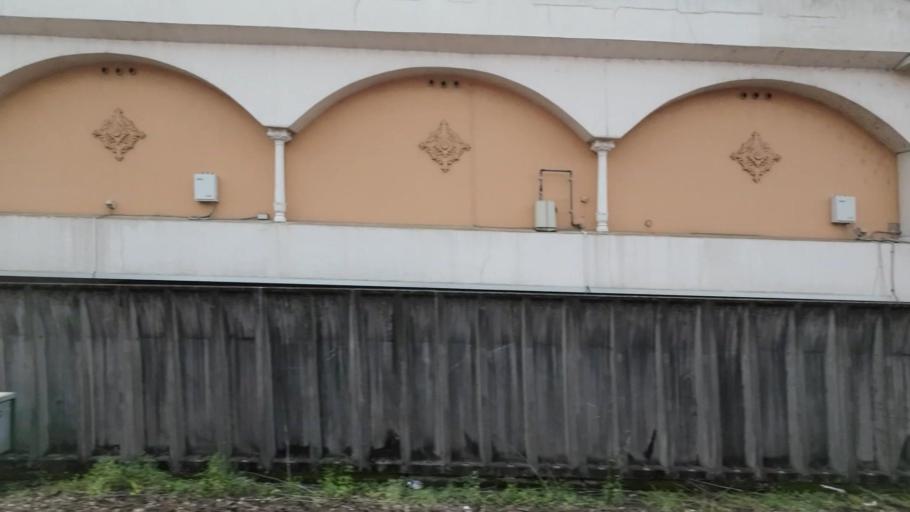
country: JP
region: Kochi
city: Kochi-shi
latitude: 33.5790
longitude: 133.5624
